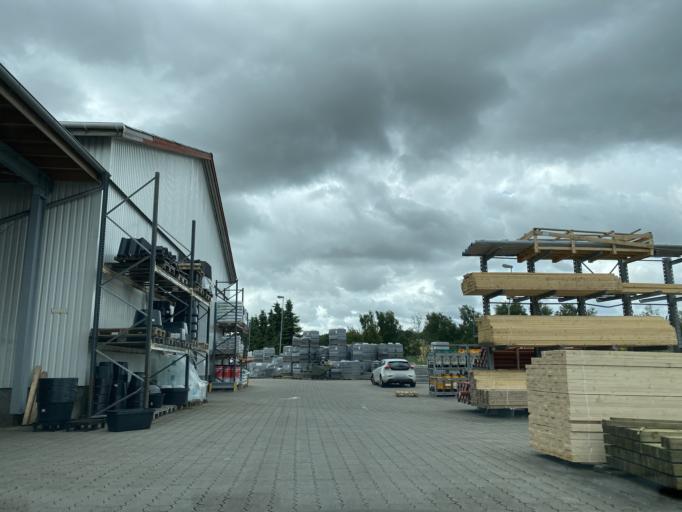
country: DK
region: Central Jutland
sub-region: Favrskov Kommune
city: Hammel
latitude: 56.2202
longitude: 9.7415
